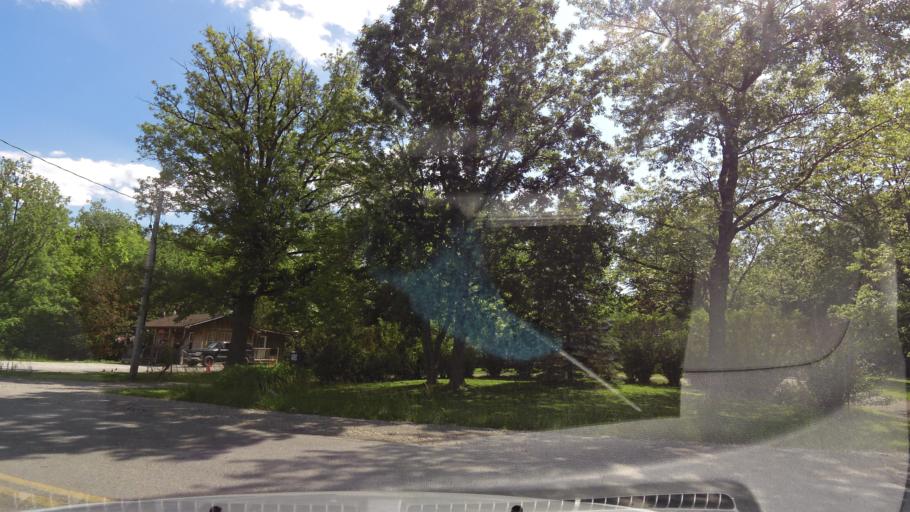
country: CA
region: Ontario
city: Ancaster
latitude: 43.1027
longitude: -80.0983
